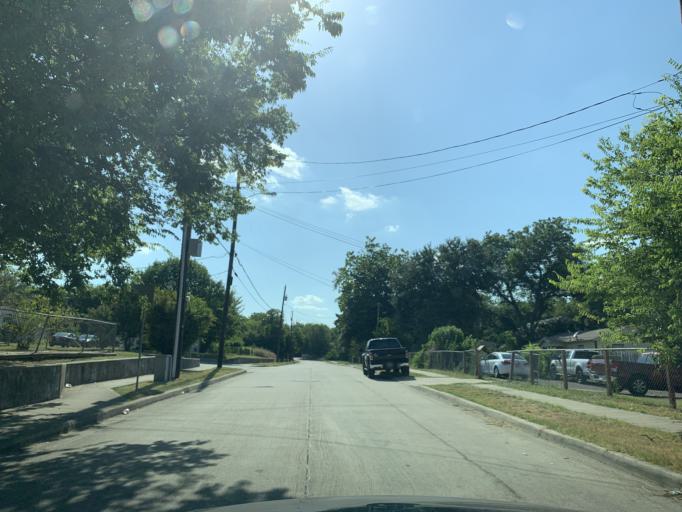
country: US
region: Texas
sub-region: Dallas County
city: Hutchins
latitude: 32.6902
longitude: -96.7740
